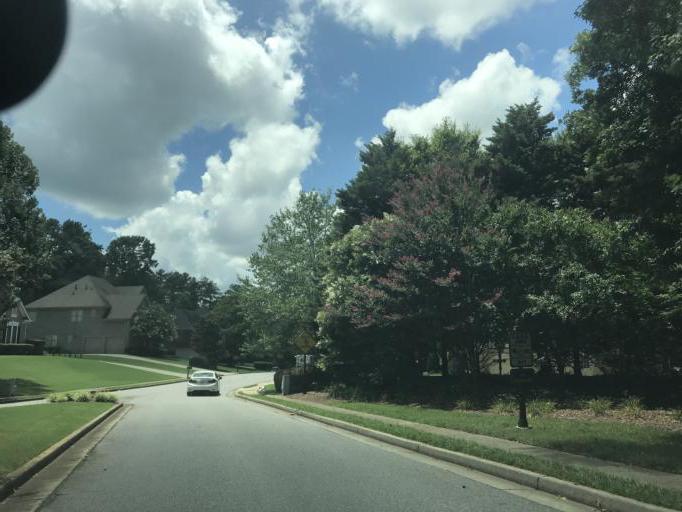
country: US
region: Georgia
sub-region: Fulton County
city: Johns Creek
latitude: 34.0754
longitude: -84.1657
